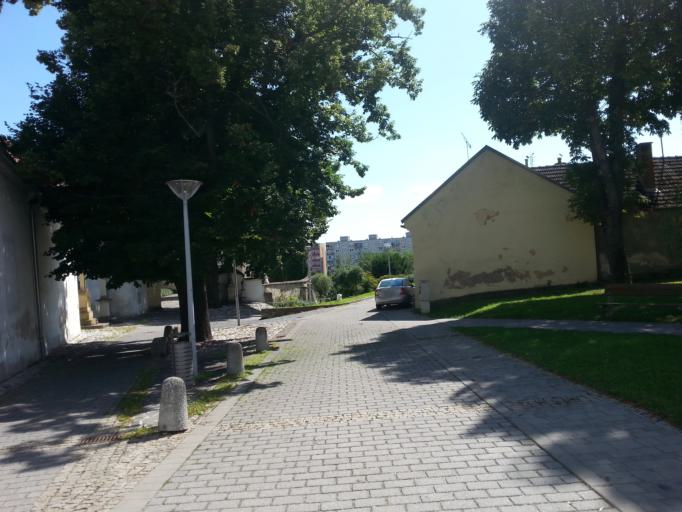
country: SK
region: Trenciansky
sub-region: Okres Nove Mesto nad Vahom
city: Nove Mesto nad Vahom
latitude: 48.7570
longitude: 17.8324
